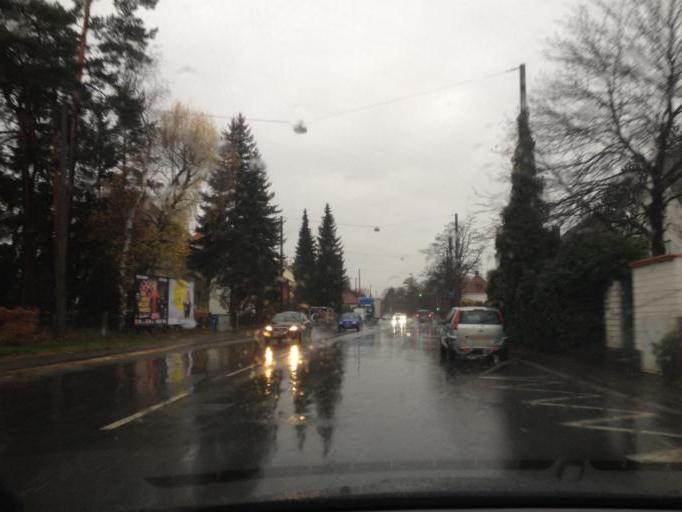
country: DE
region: Bavaria
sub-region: Regierungsbezirk Mittelfranken
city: Schwaig
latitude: 49.4689
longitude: 11.1770
